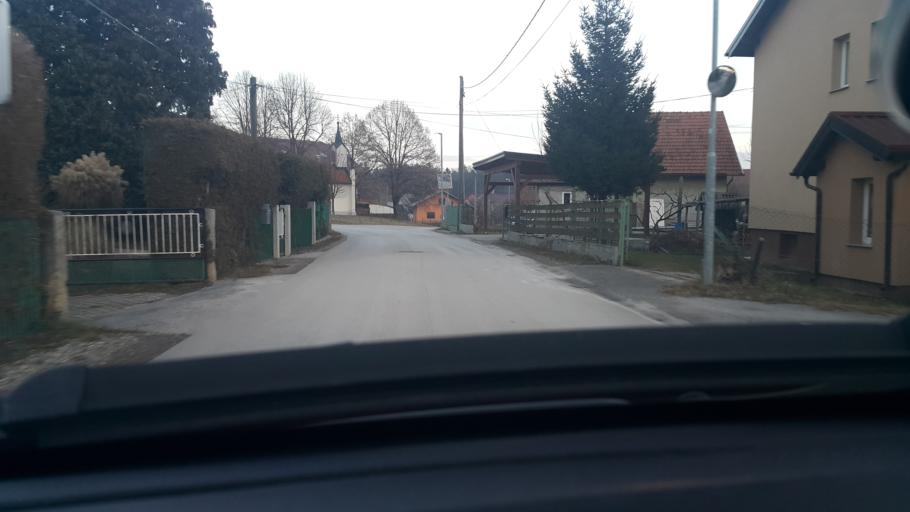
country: SI
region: Hoce-Slivnica
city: Rogoza
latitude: 46.4867
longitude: 15.6928
